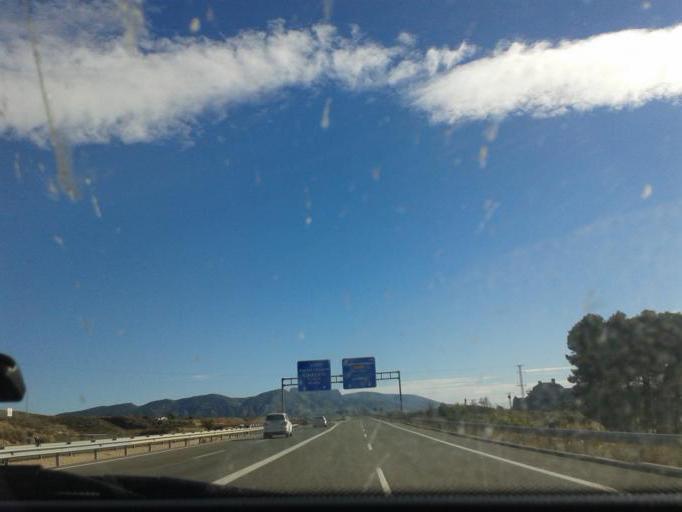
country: ES
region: Valencia
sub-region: Provincia de Alicante
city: Sax
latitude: 38.5573
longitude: -0.8266
